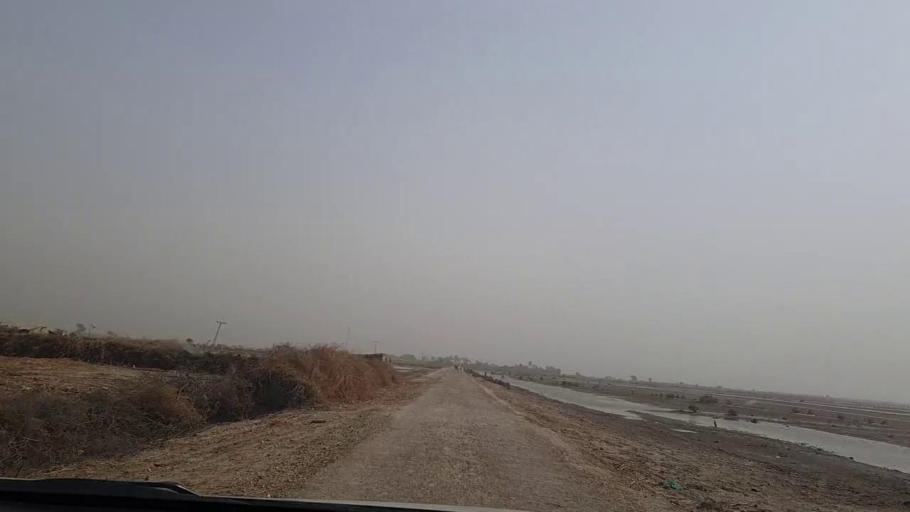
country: PK
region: Sindh
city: Pithoro
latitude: 25.4593
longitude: 69.2303
